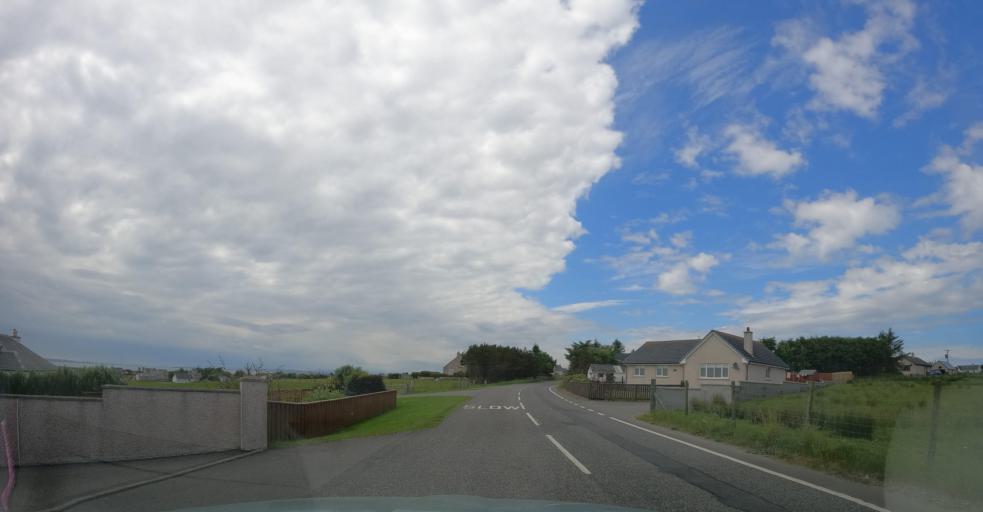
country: GB
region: Scotland
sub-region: Eilean Siar
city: Isle of Lewis
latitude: 58.2778
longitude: -6.2895
